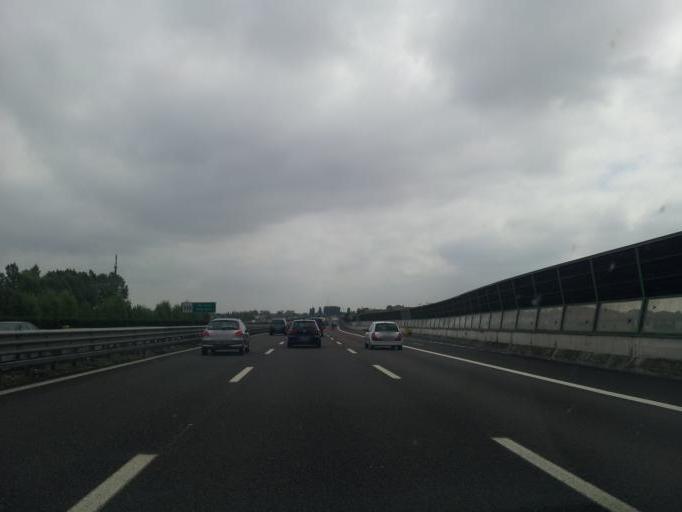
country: IT
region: Veneto
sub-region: Provincia di Vicenza
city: Arcugnano-Torri
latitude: 45.5162
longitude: 11.5682
